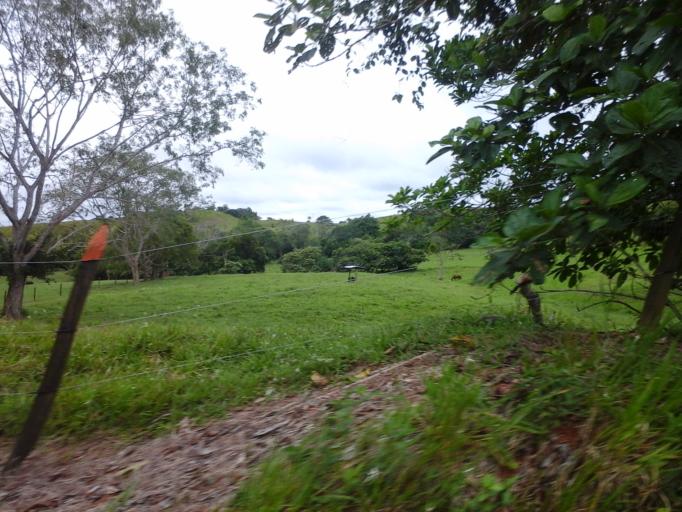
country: CO
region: Caqueta
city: El Doncello
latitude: 1.5968
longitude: -75.0332
